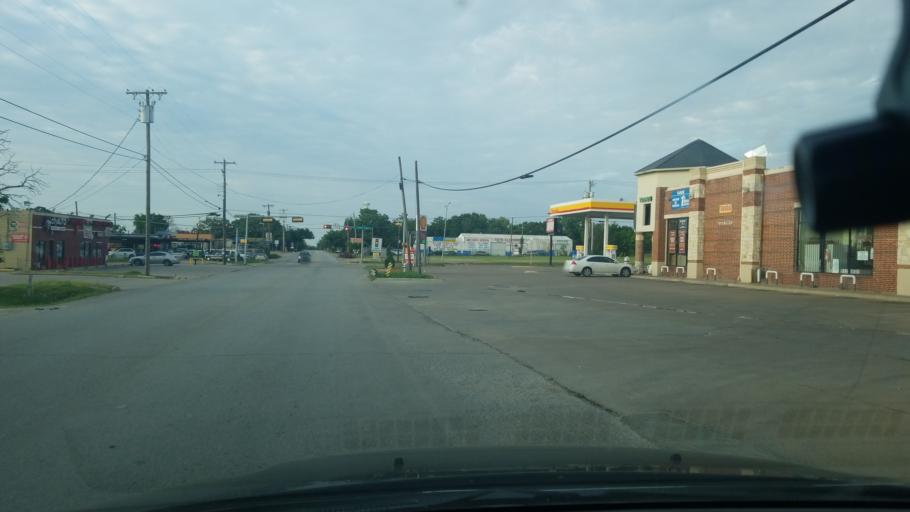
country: US
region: Texas
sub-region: Dallas County
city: Balch Springs
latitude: 32.7350
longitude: -96.6313
